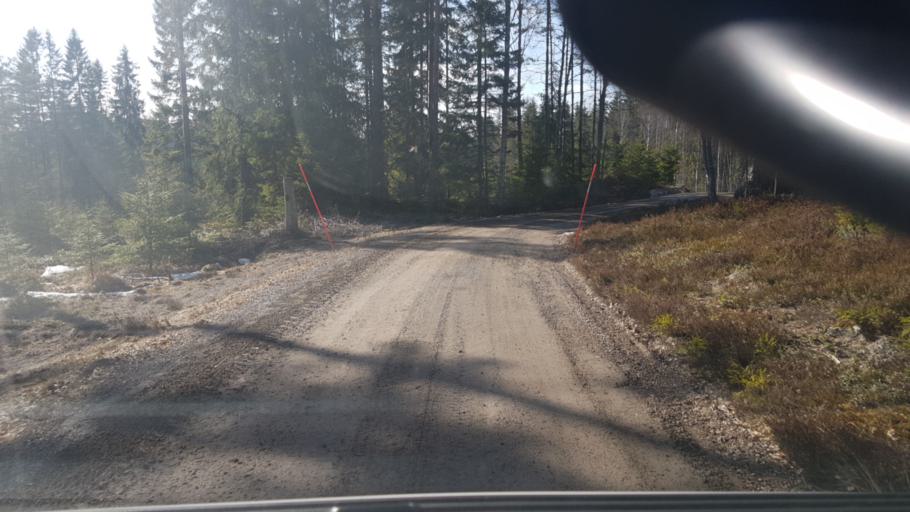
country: SE
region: Vaermland
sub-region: Eda Kommun
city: Amotfors
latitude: 59.8313
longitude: 12.3864
